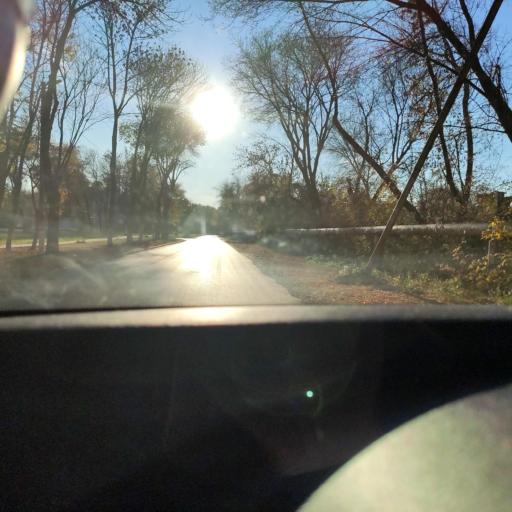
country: RU
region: Samara
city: Smyshlyayevka
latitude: 53.1904
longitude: 50.2915
